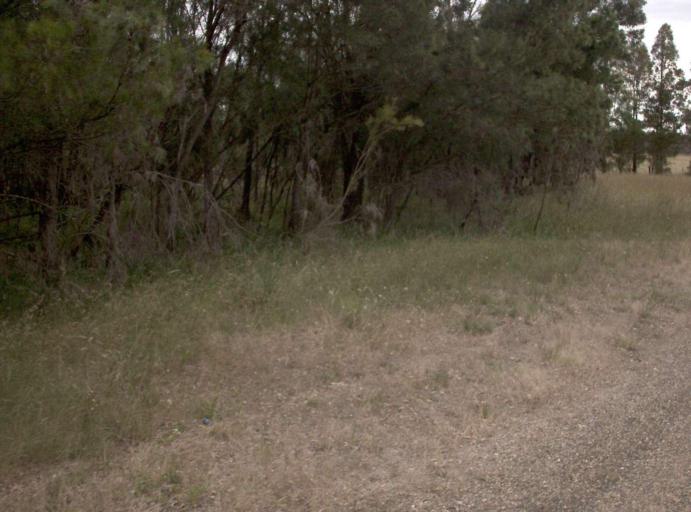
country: AU
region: Victoria
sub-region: East Gippsland
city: Bairnsdale
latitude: -37.9708
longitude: 147.4730
